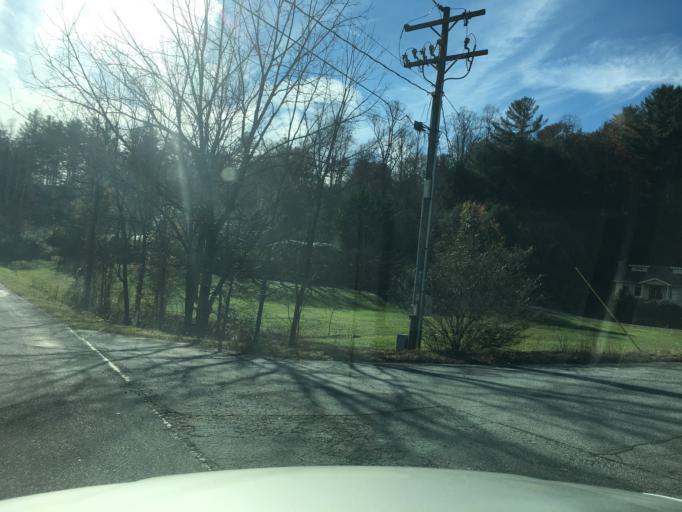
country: US
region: North Carolina
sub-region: Henderson County
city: Etowah
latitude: 35.3326
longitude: -82.6149
